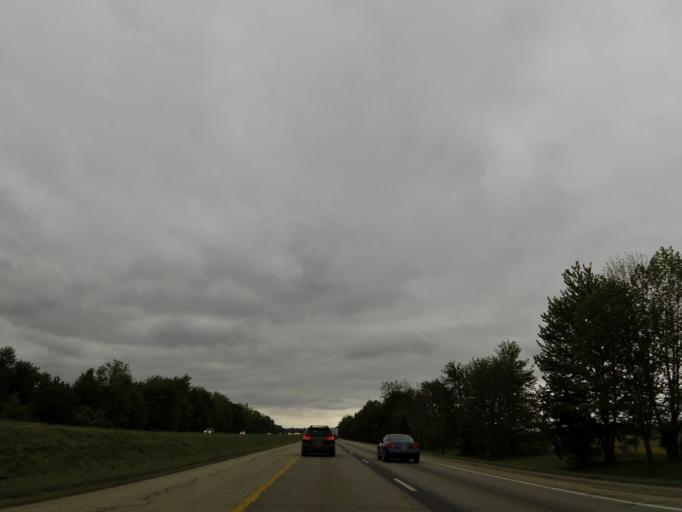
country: US
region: Ohio
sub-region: Warren County
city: Waynesville
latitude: 39.4440
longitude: -84.0399
